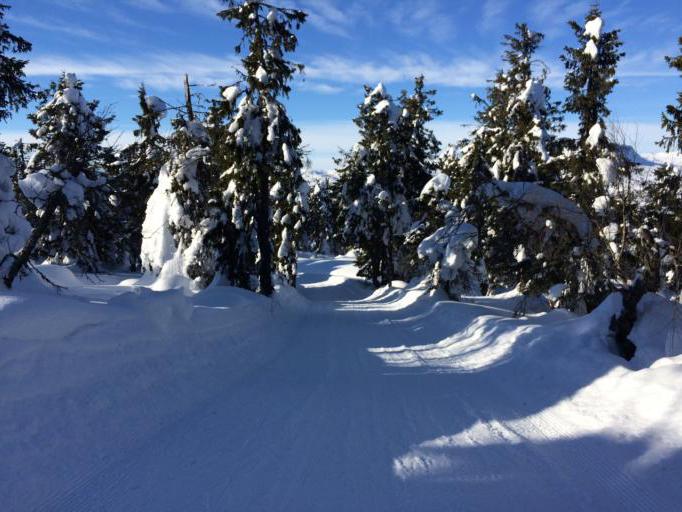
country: NO
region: Oppland
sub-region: Gausdal
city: Segalstad bru
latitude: 61.3107
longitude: 10.1044
